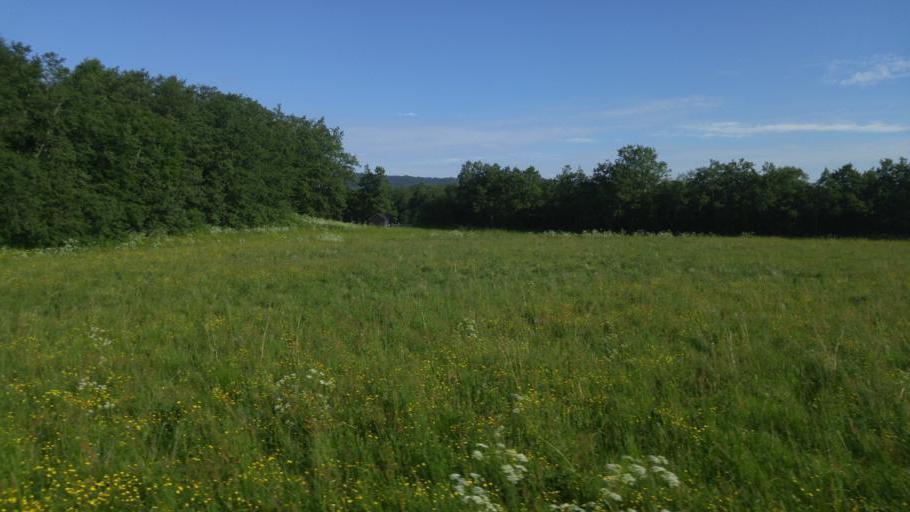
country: NO
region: Nord-Trondelag
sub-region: Stjordal
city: Stjordalshalsen
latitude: 63.4571
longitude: 11.0674
